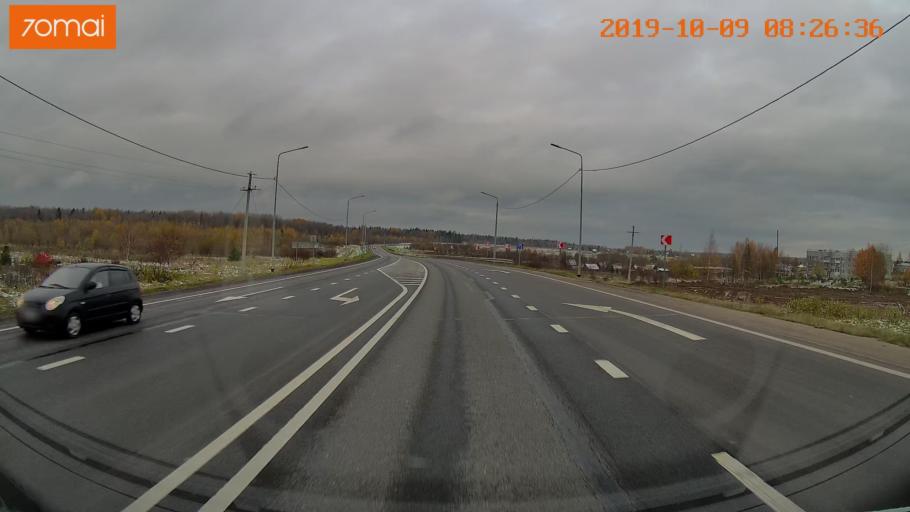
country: RU
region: Vologda
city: Gryazovets
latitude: 58.7951
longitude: 40.2636
